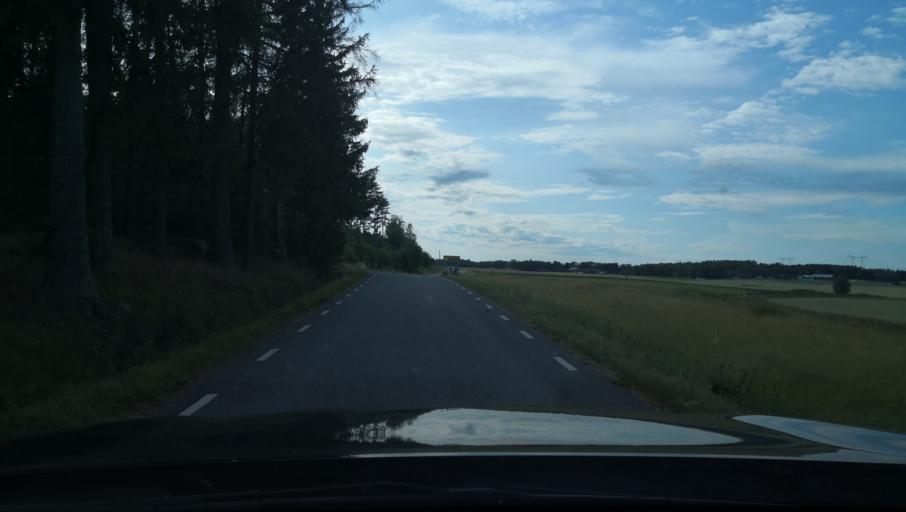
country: SE
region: Uppsala
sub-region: Enkopings Kommun
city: Orsundsbro
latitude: 59.6913
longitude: 17.3595
